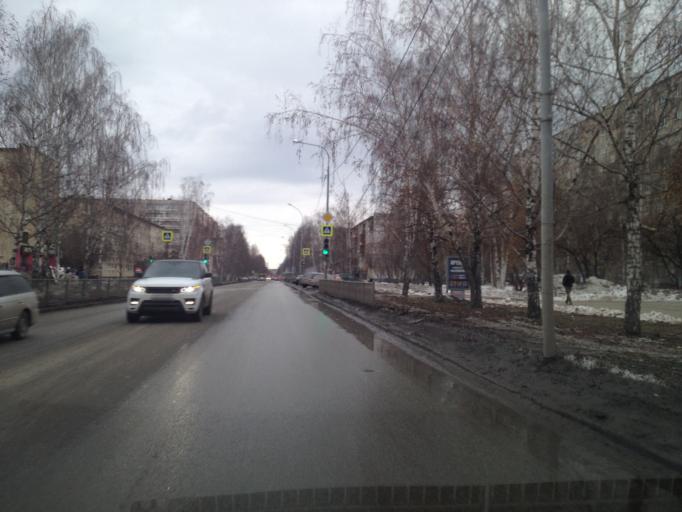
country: RU
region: Sverdlovsk
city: Sovkhoznyy
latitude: 56.8083
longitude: 60.5512
